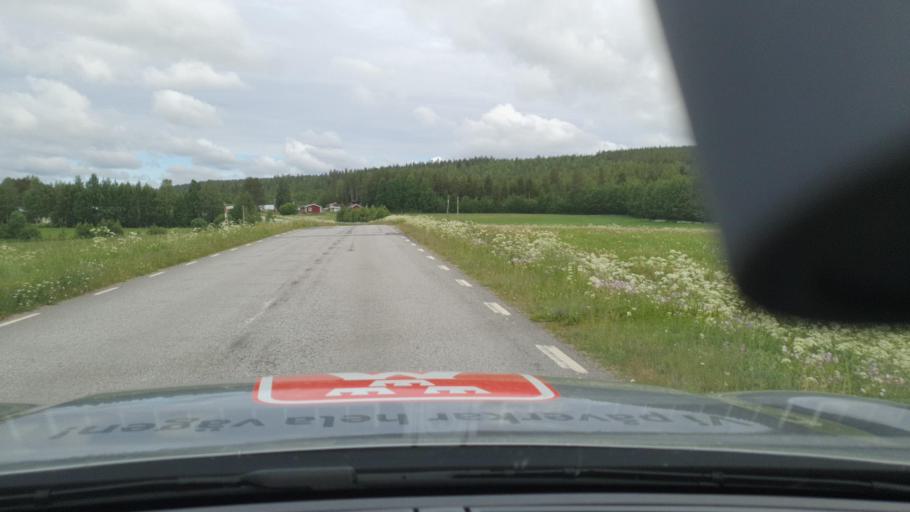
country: SE
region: Norrbotten
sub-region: Lulea Kommun
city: Ranea
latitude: 65.9743
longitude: 22.0753
